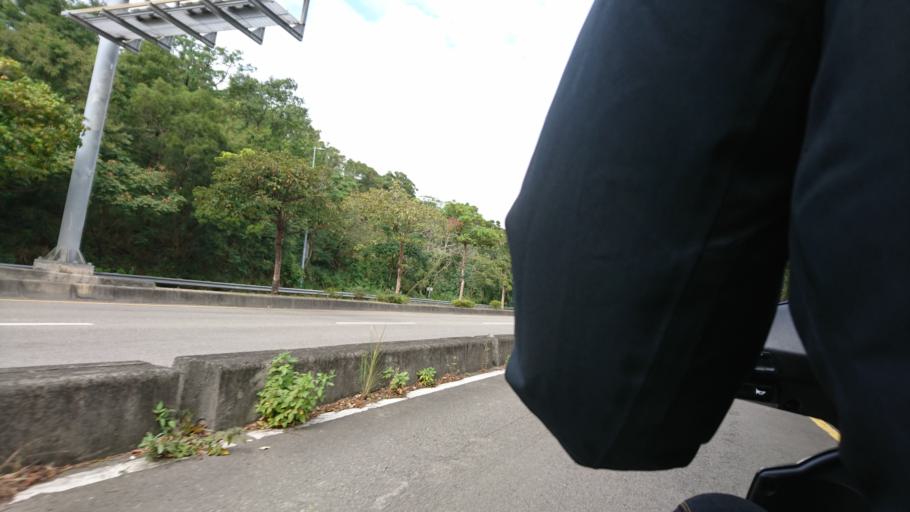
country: TW
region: Taiwan
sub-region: Hsinchu
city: Hsinchu
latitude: 24.7753
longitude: 120.9539
